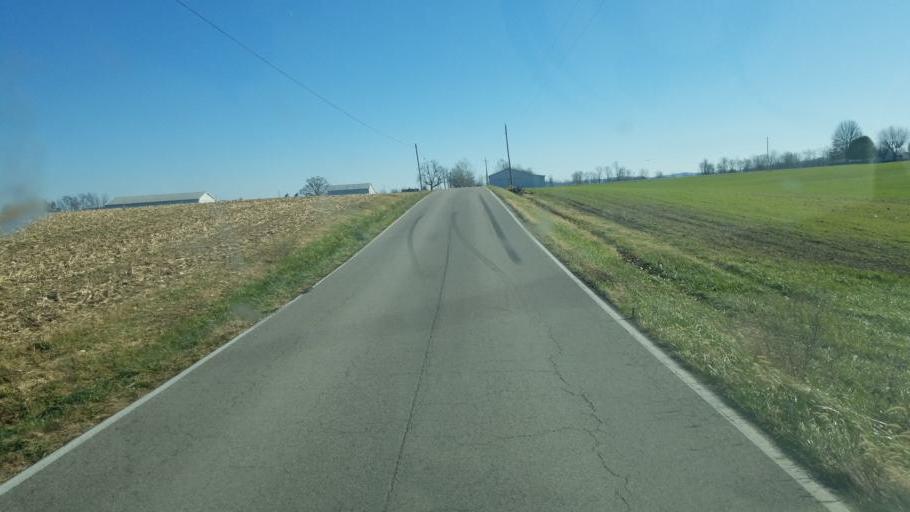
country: US
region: Ohio
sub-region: Adams County
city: Manchester
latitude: 38.5379
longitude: -83.6314
